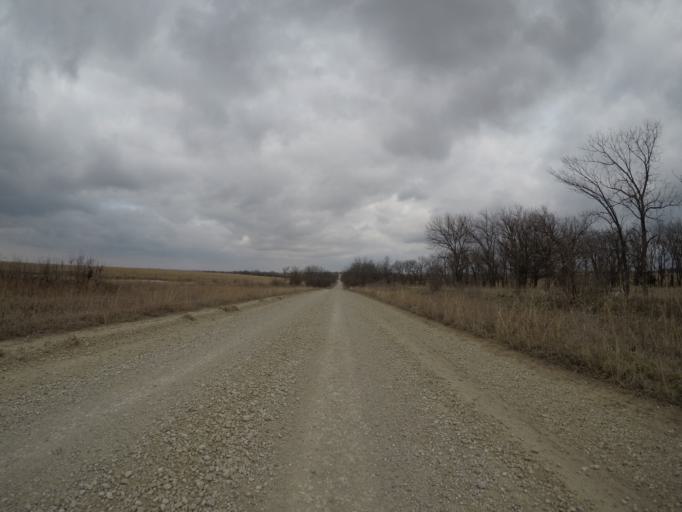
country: US
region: Kansas
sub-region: Morris County
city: Council Grove
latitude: 38.7300
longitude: -96.2796
